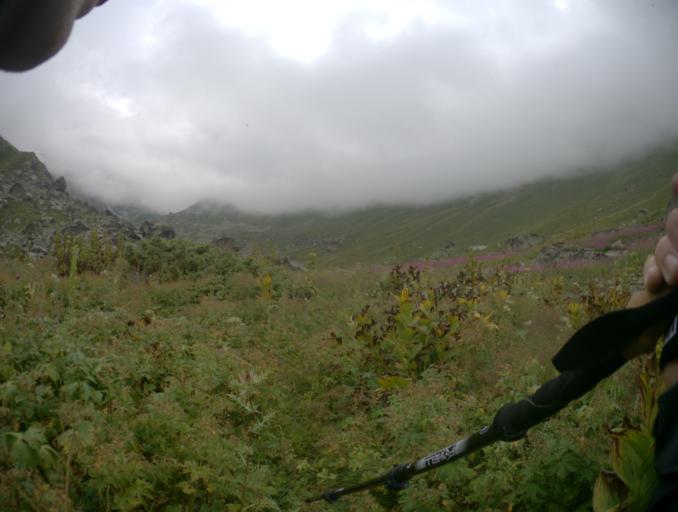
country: RU
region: Karachayevo-Cherkesiya
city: Uchkulan
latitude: 43.3336
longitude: 42.1174
